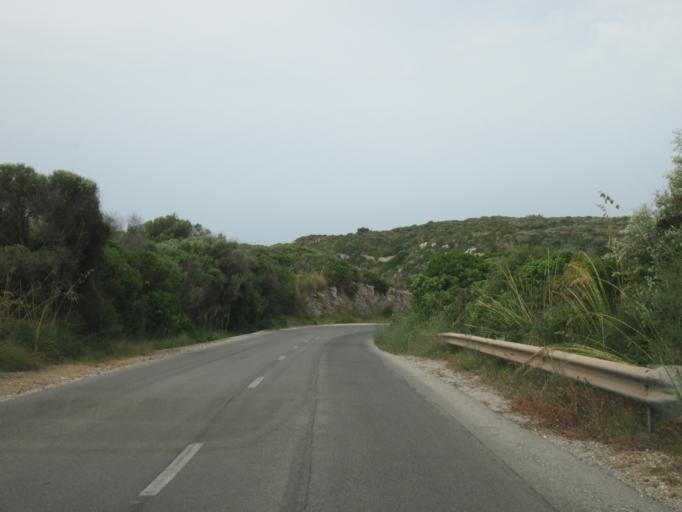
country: ES
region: Balearic Islands
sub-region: Illes Balears
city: Sant Lluis
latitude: 39.8359
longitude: 4.2053
